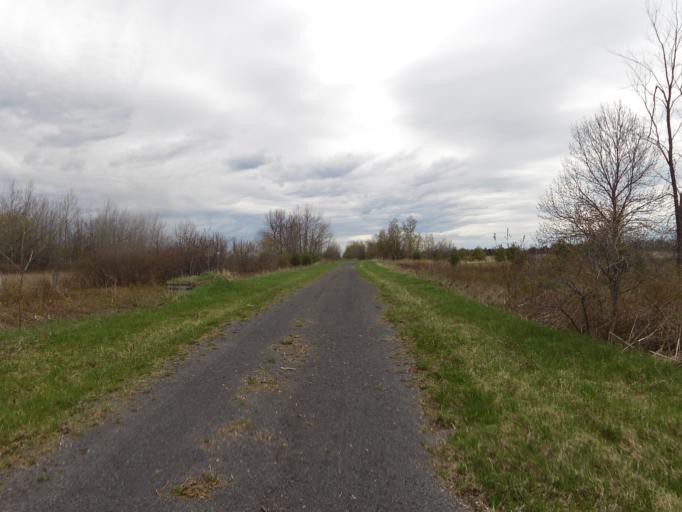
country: CA
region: Ontario
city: Hawkesbury
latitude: 45.5443
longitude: -74.7946
